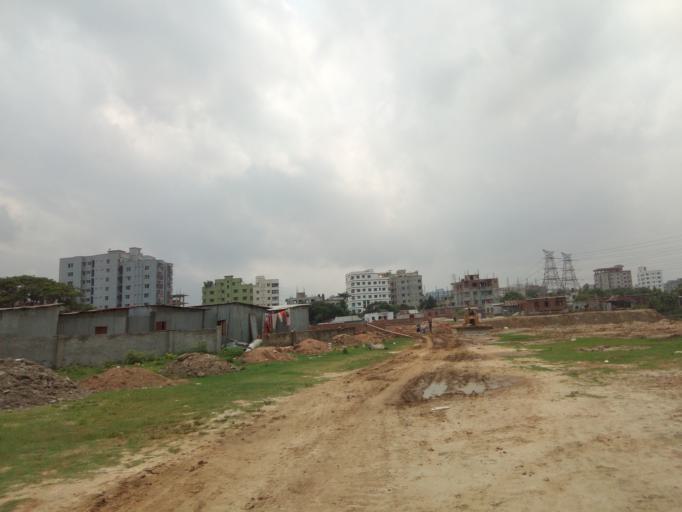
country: BD
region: Dhaka
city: Paltan
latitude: 23.7682
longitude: 90.4364
